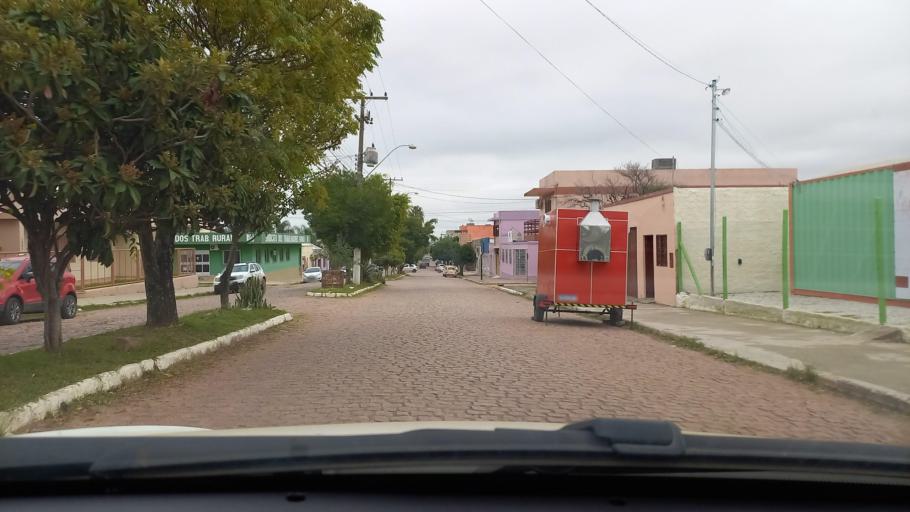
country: BR
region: Rio Grande do Sul
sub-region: Dom Pedrito
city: Dom Pedrito
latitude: -30.9798
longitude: -54.6688
